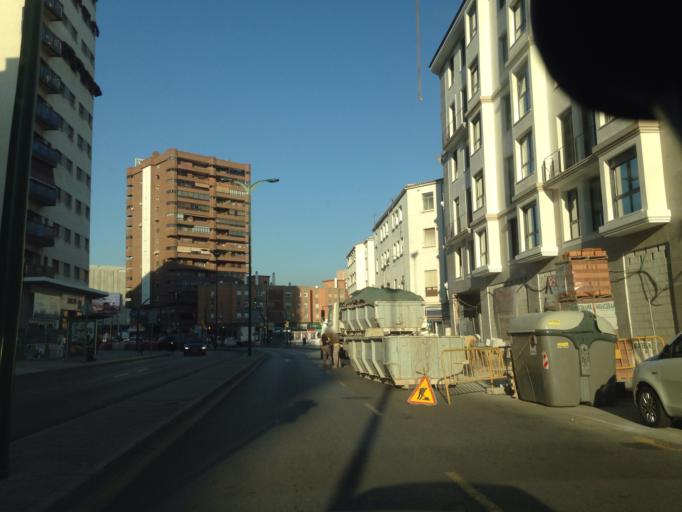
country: ES
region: Andalusia
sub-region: Provincia de Malaga
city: Malaga
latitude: 36.7149
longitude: -4.4303
